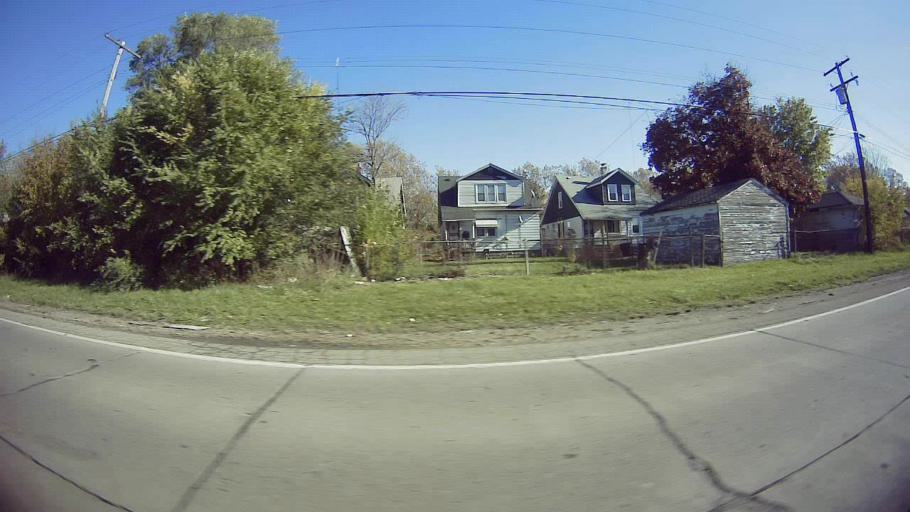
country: US
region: Michigan
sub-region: Wayne County
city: Hamtramck
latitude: 42.4133
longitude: -83.0424
